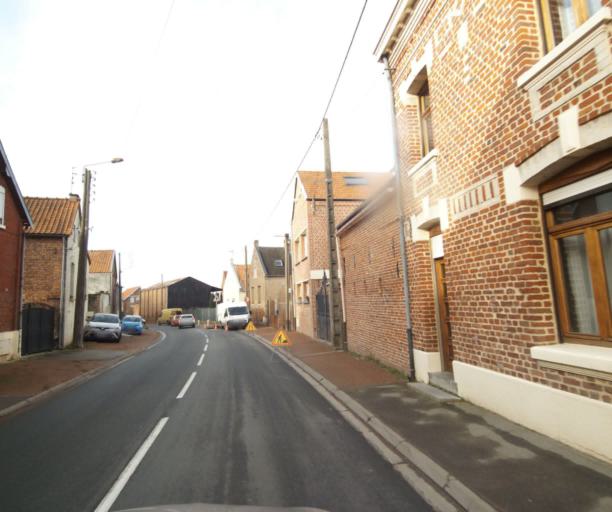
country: FR
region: Nord-Pas-de-Calais
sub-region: Departement du Nord
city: Vendegies-sur-Ecaillon
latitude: 50.2659
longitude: 3.4773
